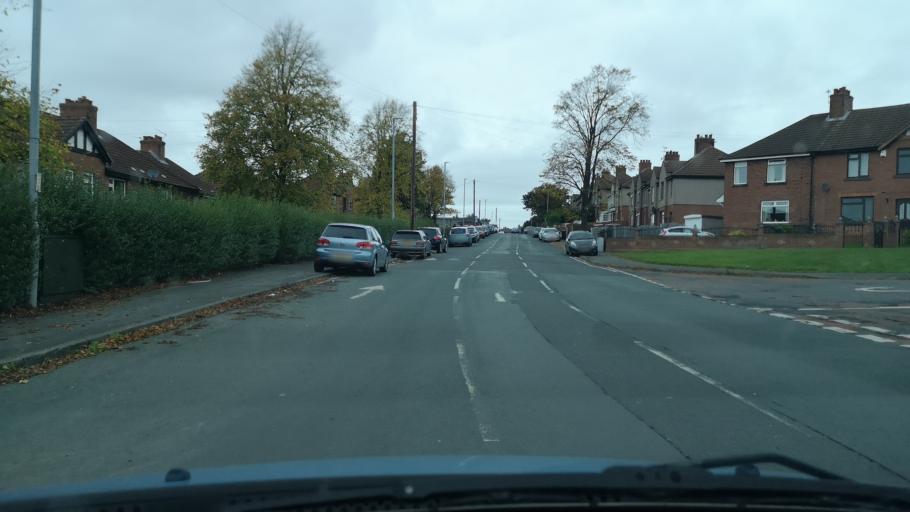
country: GB
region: England
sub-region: Kirklees
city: Dewsbury
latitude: 53.6853
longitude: -1.6545
